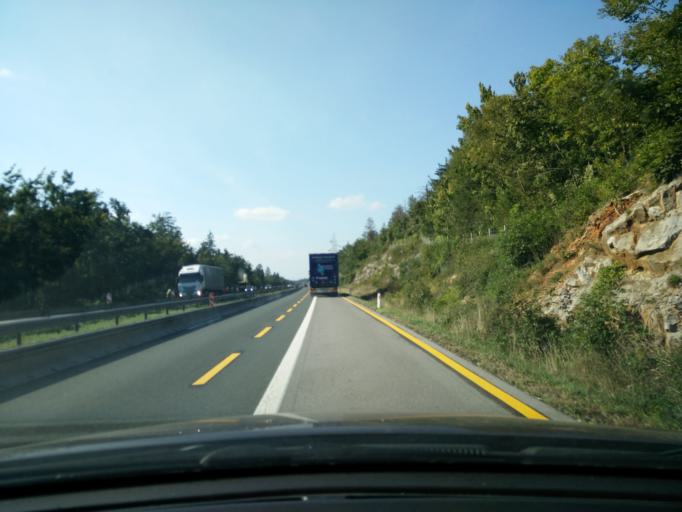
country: SI
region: Cerknica
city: Rakek
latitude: 45.8525
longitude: 14.2826
